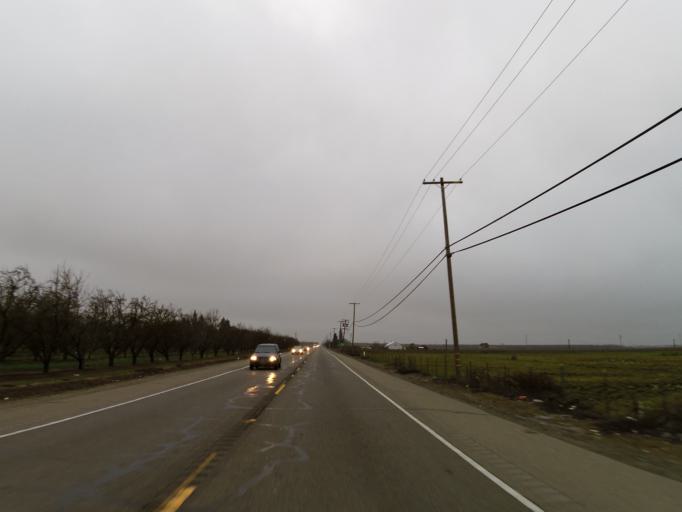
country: US
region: California
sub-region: Stanislaus County
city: Riverdale Park
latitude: 37.6381
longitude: -121.0997
